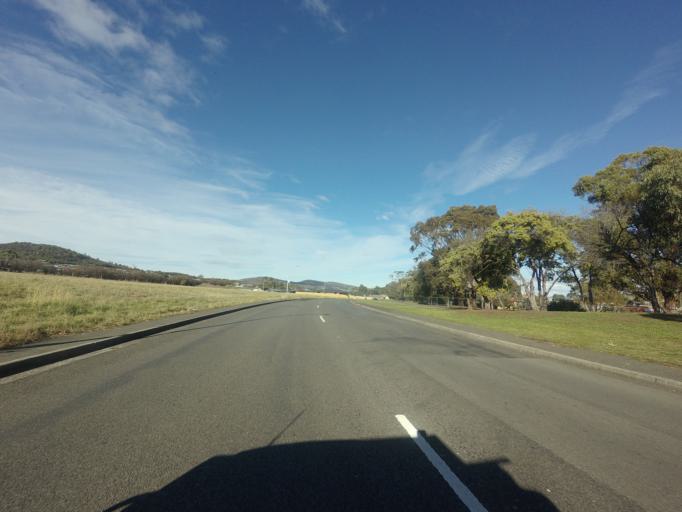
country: AU
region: Tasmania
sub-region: Clarence
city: Rokeby
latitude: -42.8960
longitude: 147.4466
